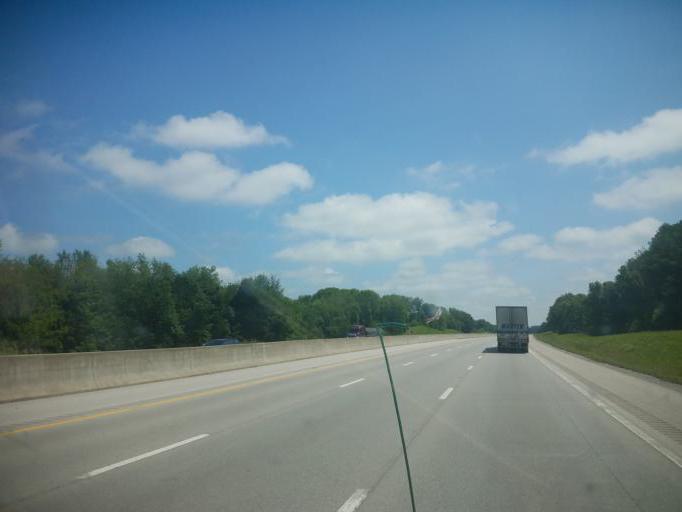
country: US
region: Kentucky
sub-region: Barren County
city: Cave City
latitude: 37.0763
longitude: -86.0803
